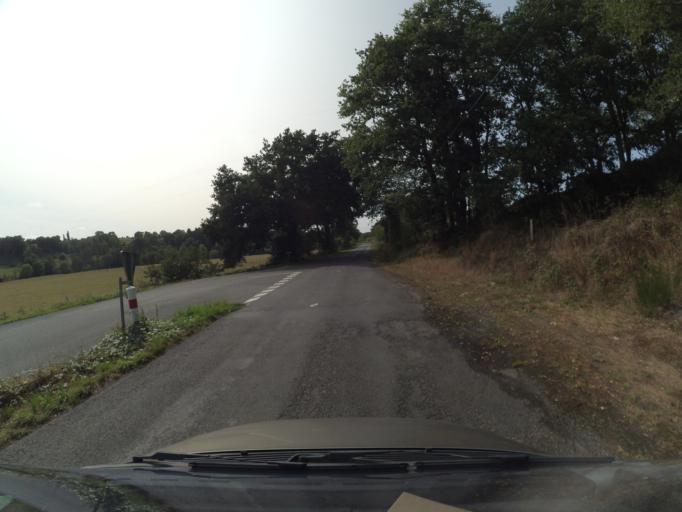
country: FR
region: Pays de la Loire
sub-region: Departement de Maine-et-Loire
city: Torfou
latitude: 47.0267
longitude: -1.1402
